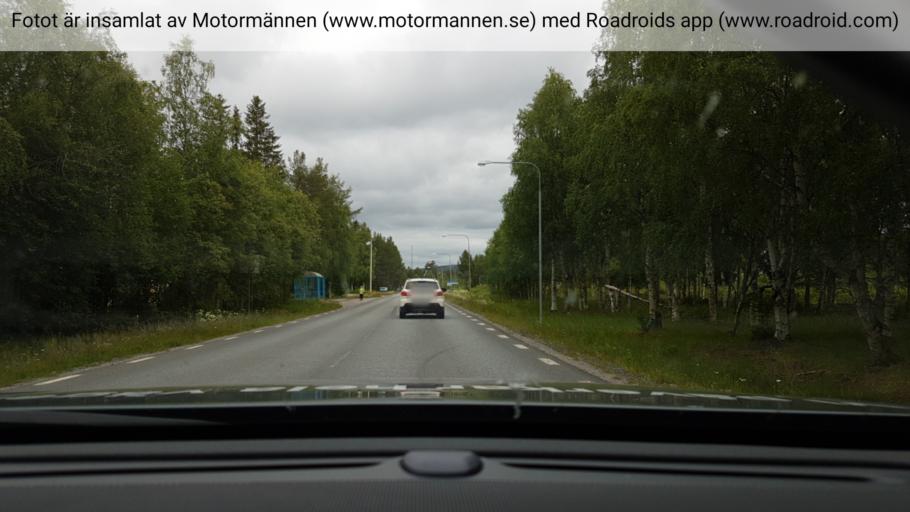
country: SE
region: Vaesterbotten
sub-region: Sorsele Kommun
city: Sorsele
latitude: 65.5256
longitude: 17.5389
